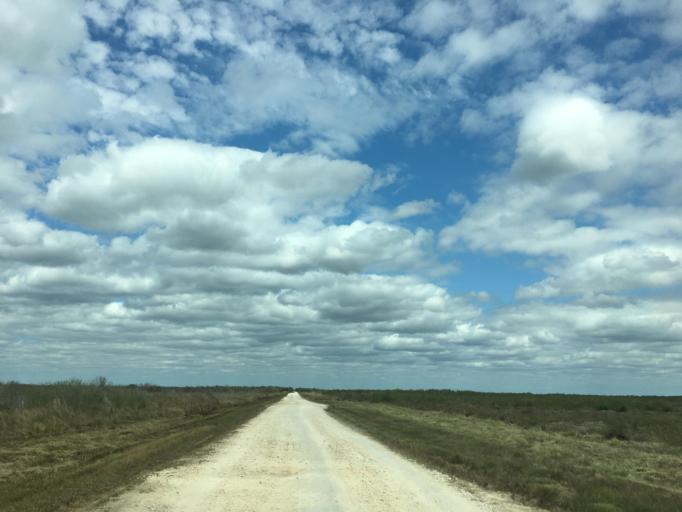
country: US
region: Texas
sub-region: Brazoria County
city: Oyster Creek
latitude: 29.0442
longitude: -95.2682
